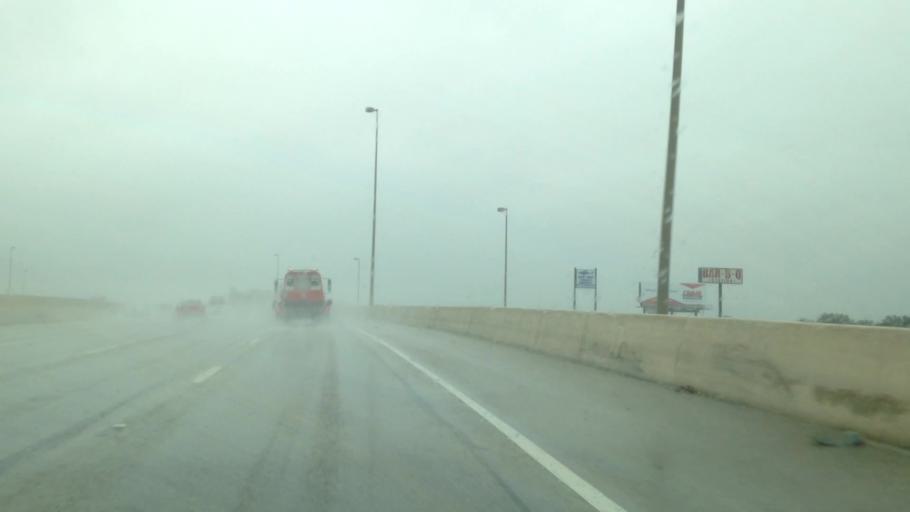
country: US
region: Texas
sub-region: Bexar County
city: Alamo Heights
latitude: 29.5155
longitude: -98.4404
